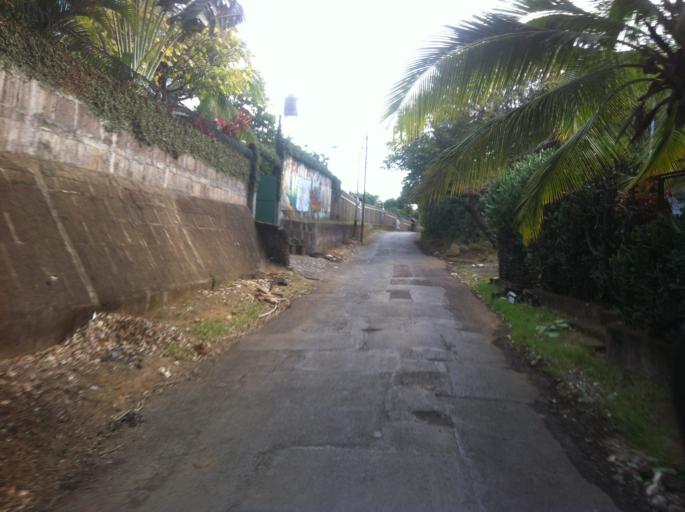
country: NI
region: Managua
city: Ciudad Sandino
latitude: 12.1010
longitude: -86.3122
